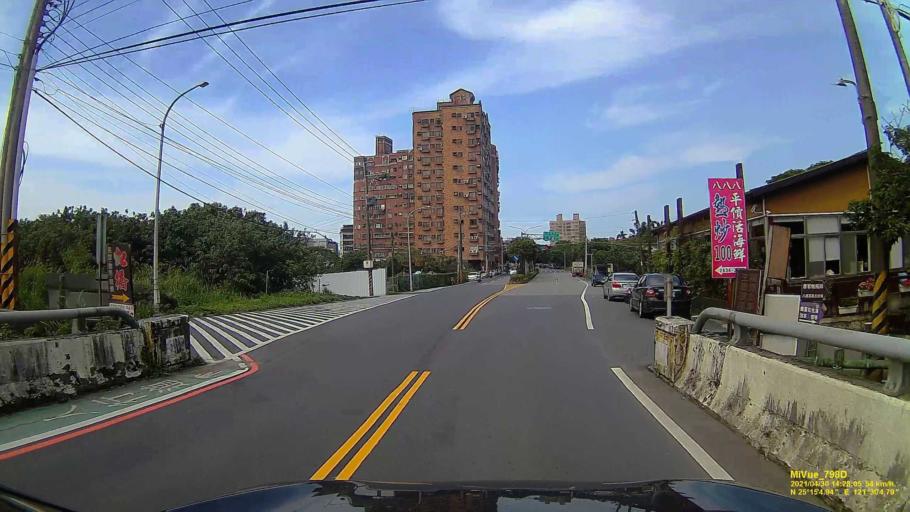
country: TW
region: Taipei
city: Taipei
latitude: 25.2516
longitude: 121.5014
